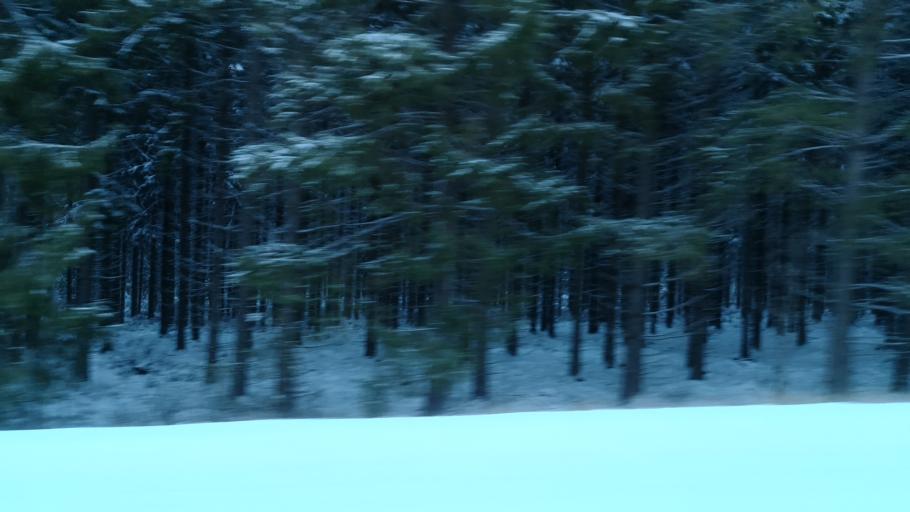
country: FI
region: Southern Savonia
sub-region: Savonlinna
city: Enonkoski
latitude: 62.0747
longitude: 28.7170
